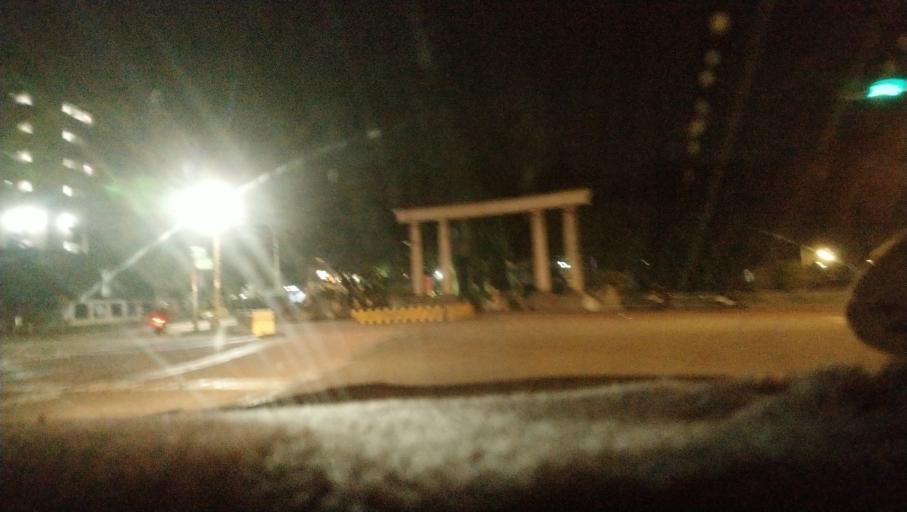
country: TW
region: Taiwan
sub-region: Yunlin
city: Douliu
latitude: 23.7015
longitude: 120.4308
